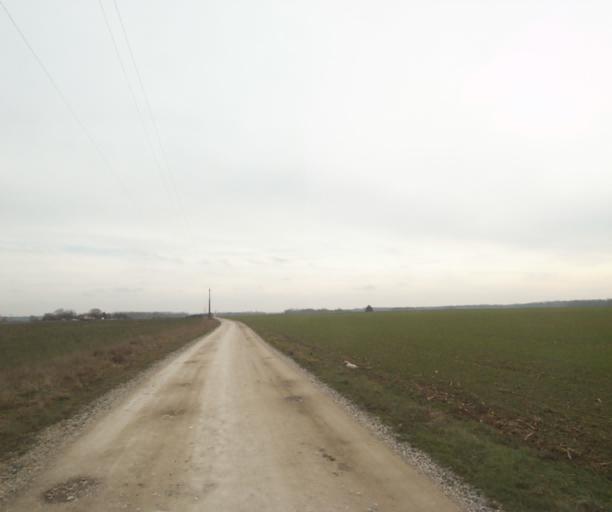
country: FR
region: Champagne-Ardenne
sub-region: Departement de la Haute-Marne
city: Villiers-en-Lieu
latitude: 48.6761
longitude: 4.8665
